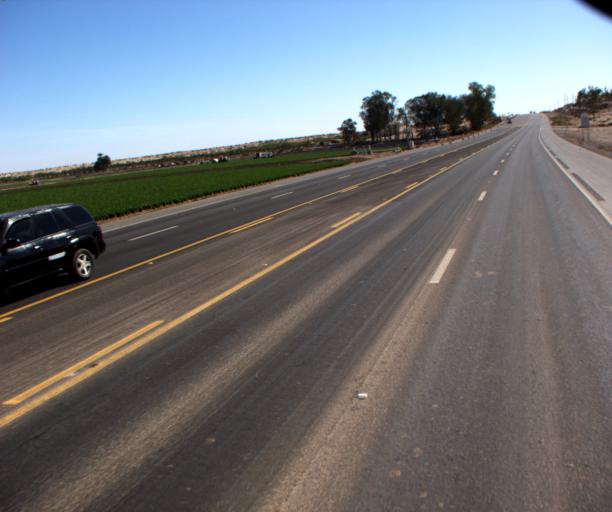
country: US
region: Arizona
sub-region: Yuma County
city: Somerton
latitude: 32.5967
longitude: -114.6805
